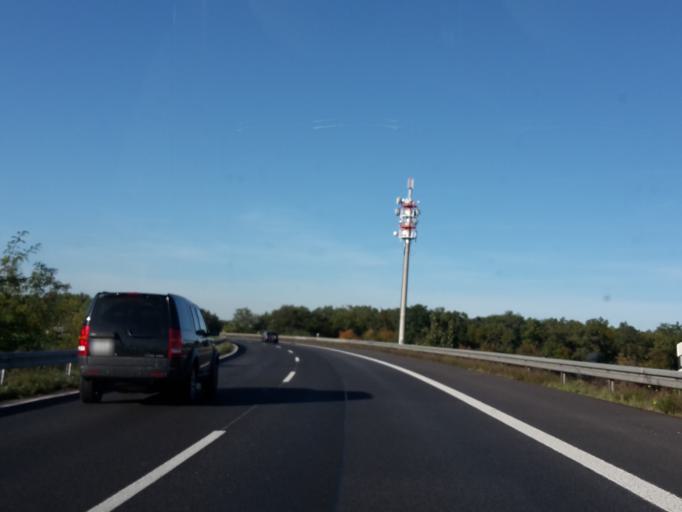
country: DE
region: Hesse
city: Viernheim
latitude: 49.5521
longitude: 8.5598
